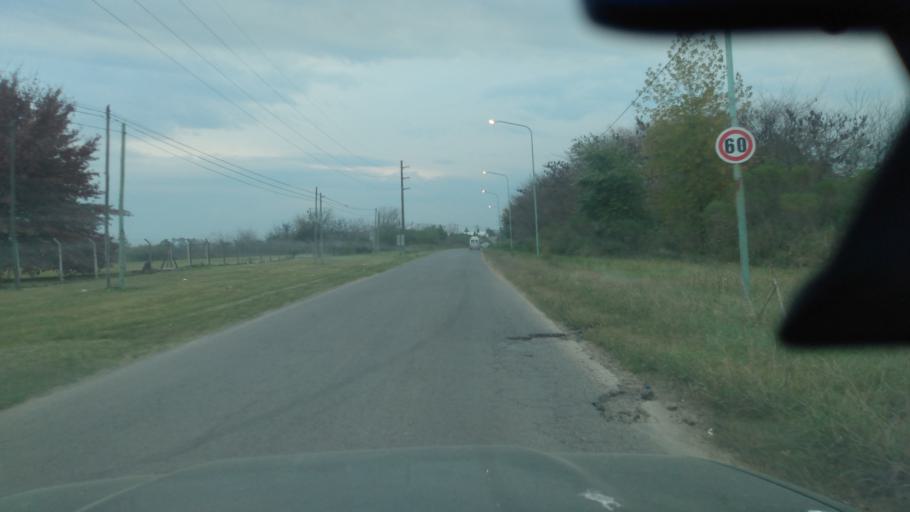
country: AR
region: Buenos Aires
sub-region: Partido de Lujan
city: Lujan
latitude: -34.5647
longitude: -59.1421
